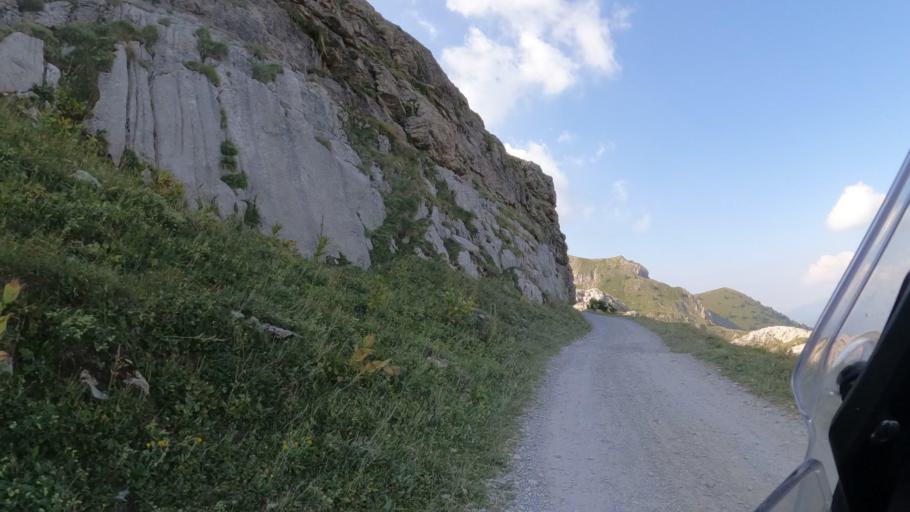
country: IT
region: Piedmont
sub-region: Provincia di Cuneo
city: Limone Piemonte
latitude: 44.1624
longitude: 7.6698
